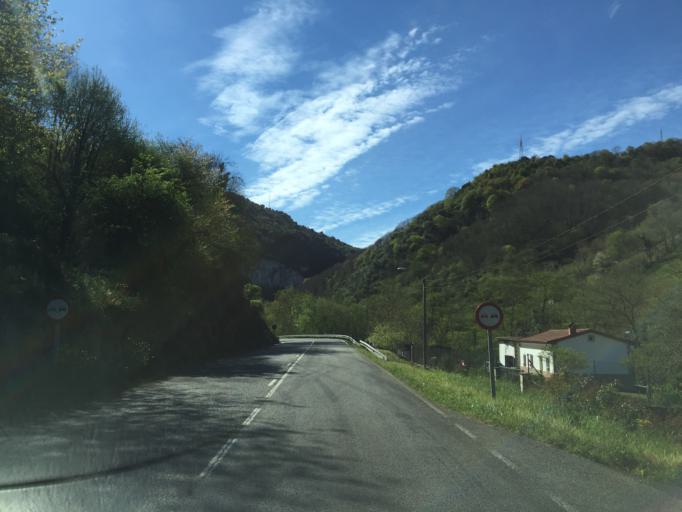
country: ES
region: Asturias
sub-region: Province of Asturias
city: Proaza
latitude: 43.3106
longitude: -5.9877
